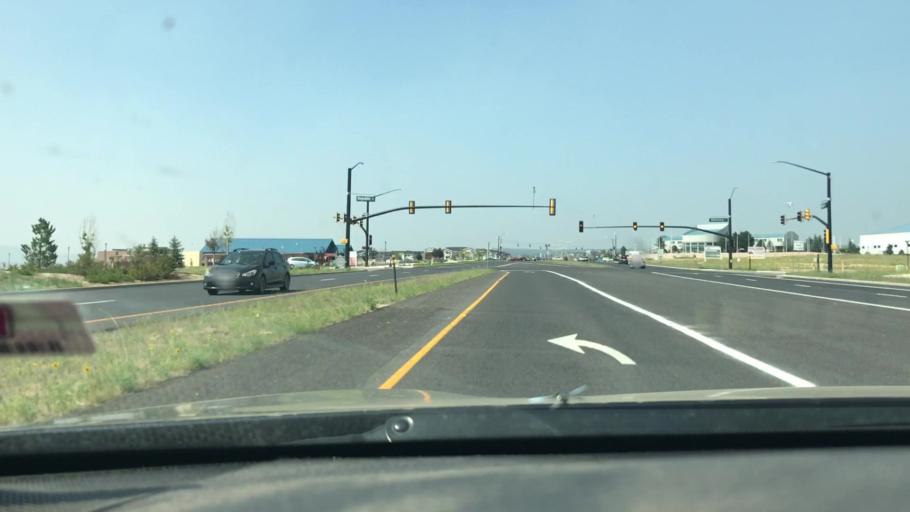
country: US
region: Colorado
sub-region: El Paso County
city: Gleneagle
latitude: 38.9874
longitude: -104.7980
